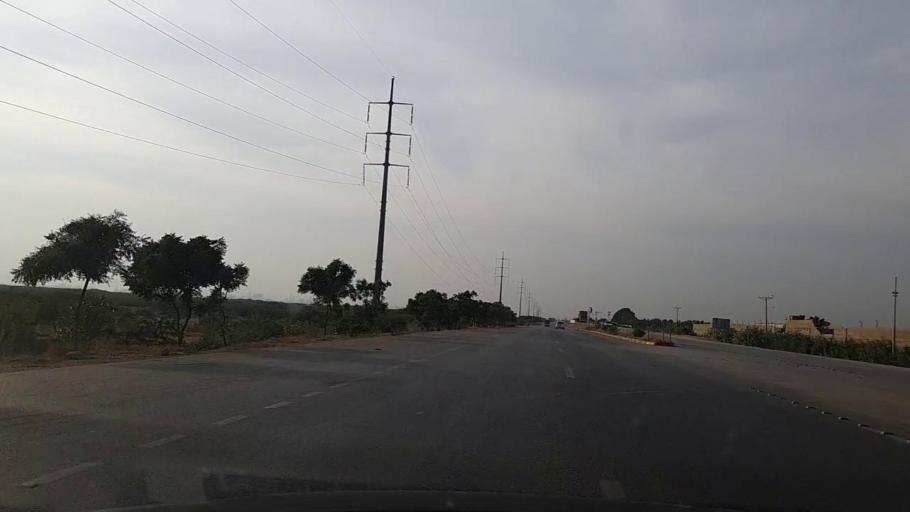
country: PK
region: Sindh
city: Gharo
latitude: 24.8285
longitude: 67.4684
